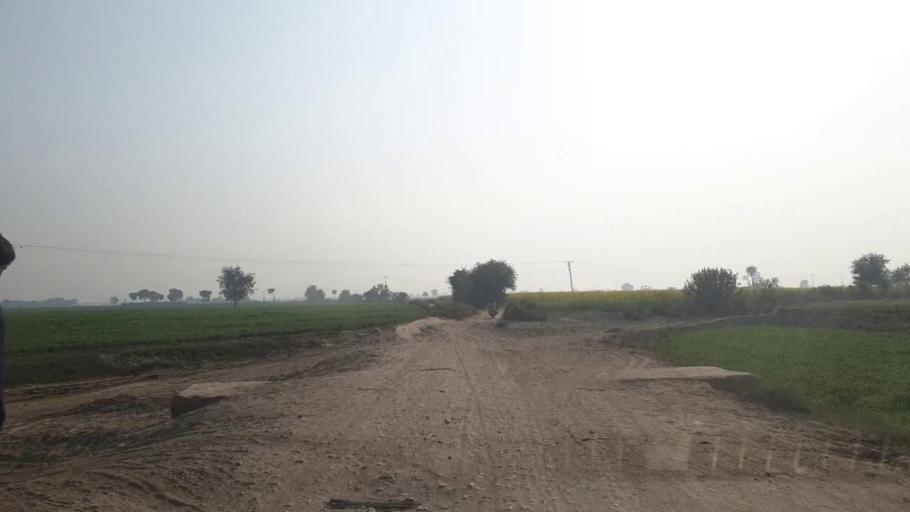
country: PK
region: Sindh
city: Hala
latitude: 25.7596
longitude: 68.3836
